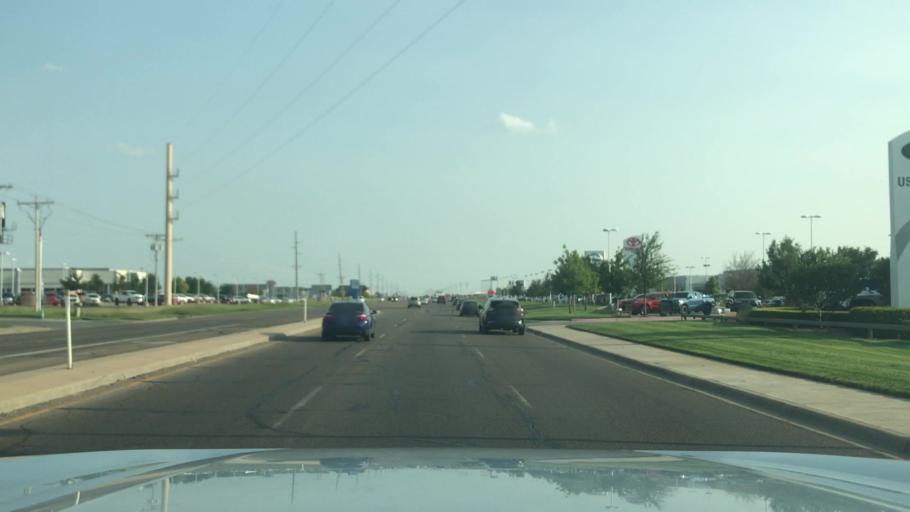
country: US
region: Texas
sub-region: Potter County
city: Amarillo
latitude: 35.1613
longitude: -101.9382
